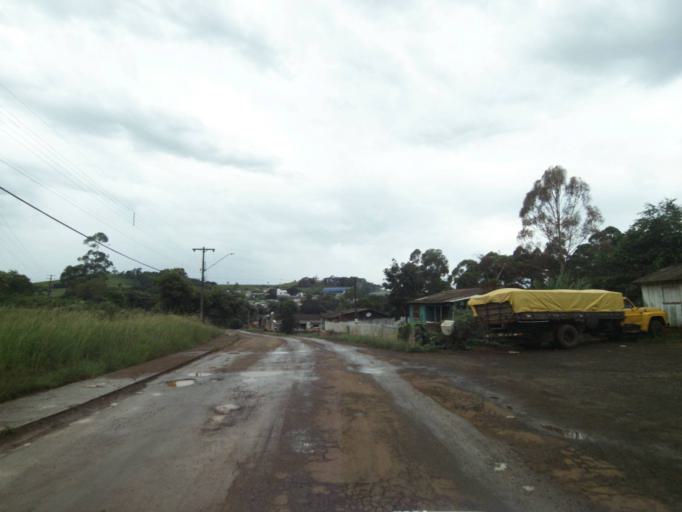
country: BR
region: Parana
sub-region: Guaraniacu
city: Guaraniacu
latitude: -25.1099
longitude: -52.8545
